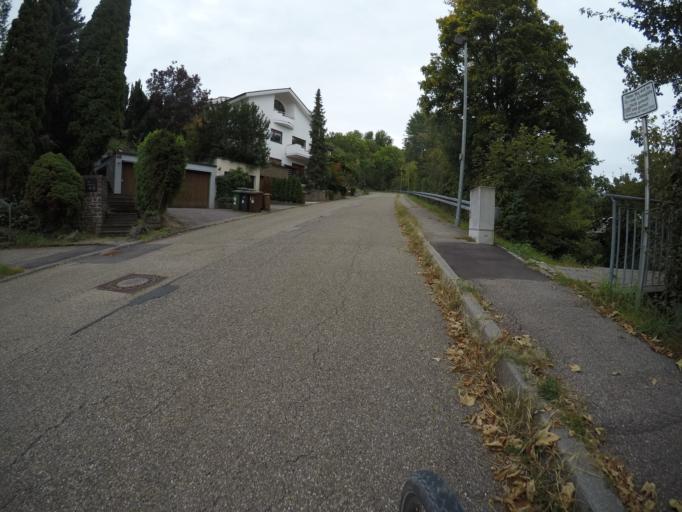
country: DE
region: Baden-Wuerttemberg
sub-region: Regierungsbezirk Stuttgart
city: Eberdingen
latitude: 48.8919
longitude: 8.9682
